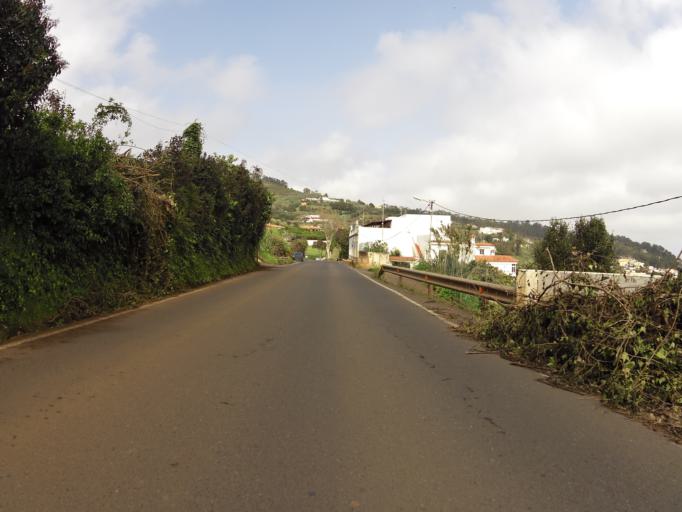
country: ES
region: Canary Islands
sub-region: Provincia de Las Palmas
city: Teror
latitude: 28.0790
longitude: -15.5409
